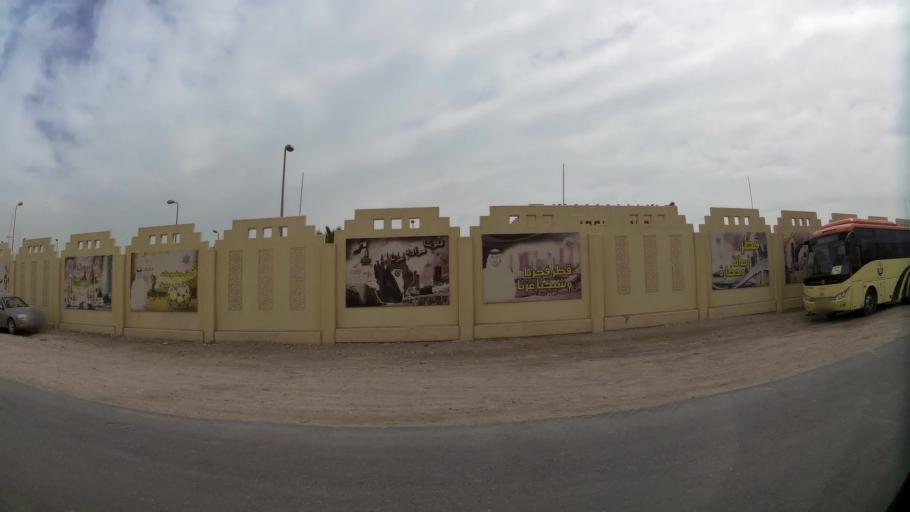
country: QA
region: Baladiyat ad Dawhah
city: Doha
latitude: 25.2121
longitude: 51.4736
